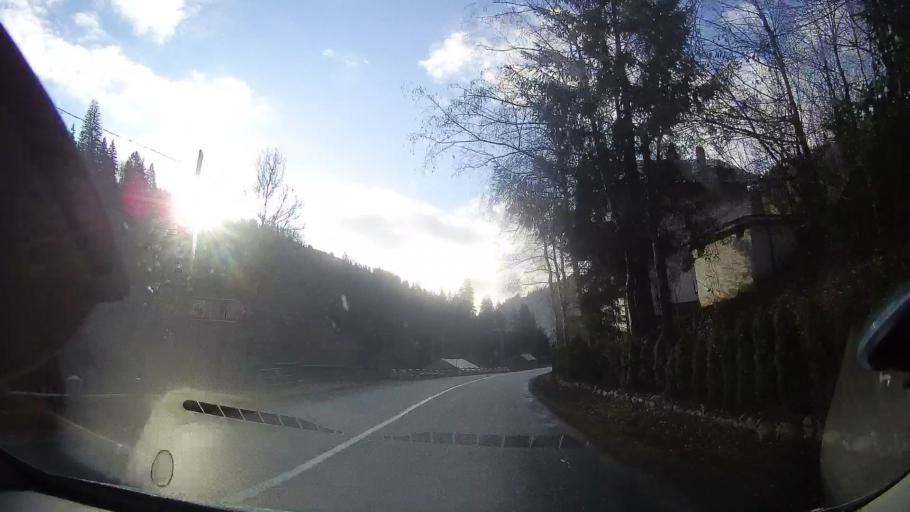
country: RO
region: Alba
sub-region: Comuna Albac
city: Albac
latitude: 46.4336
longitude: 22.9663
